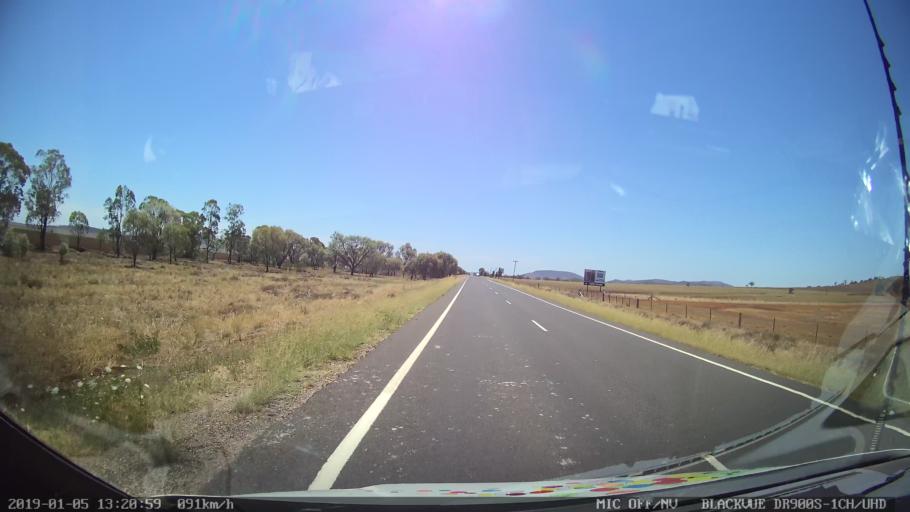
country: AU
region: New South Wales
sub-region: Gunnedah
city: Gunnedah
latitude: -31.0980
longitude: 149.9428
